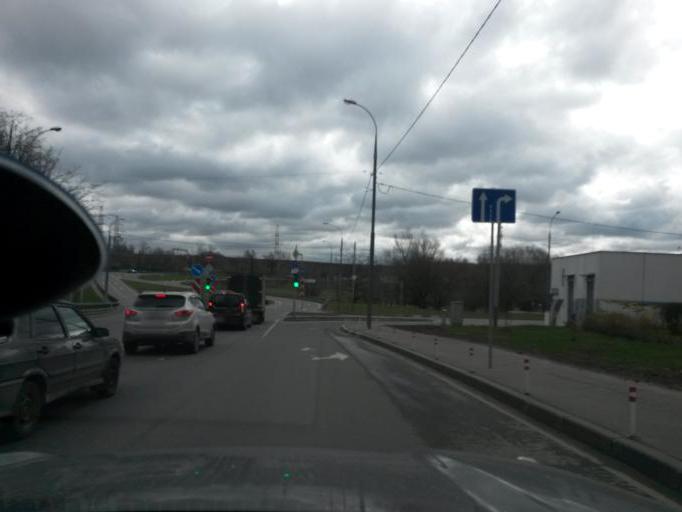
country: RU
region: Moscow
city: Annino
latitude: 55.5610
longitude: 37.5878
